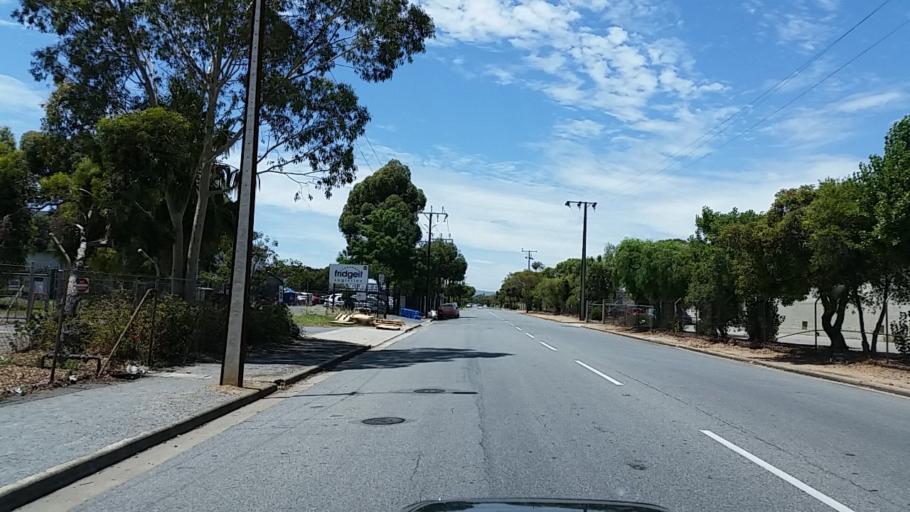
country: AU
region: South Australia
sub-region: Charles Sturt
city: Woodville North
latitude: -34.8628
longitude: 138.5392
